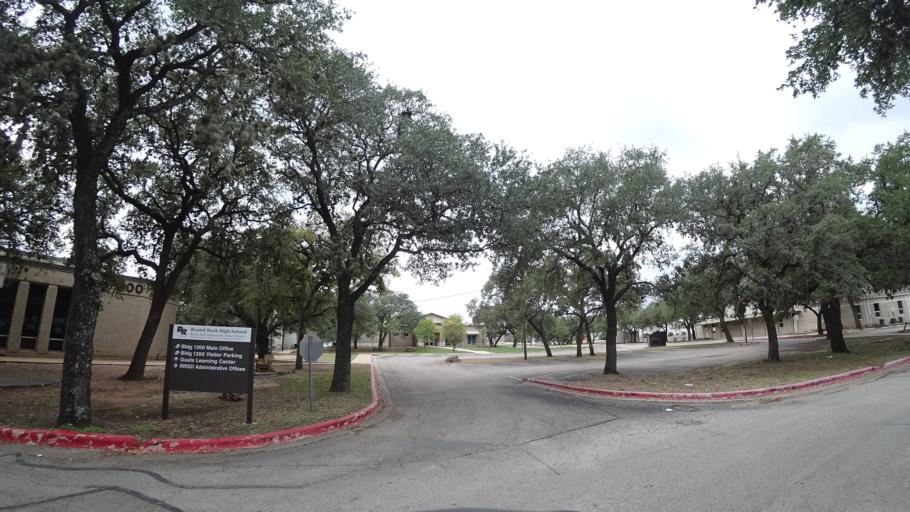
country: US
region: Texas
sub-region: Williamson County
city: Round Rock
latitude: 30.5101
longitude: -97.6967
